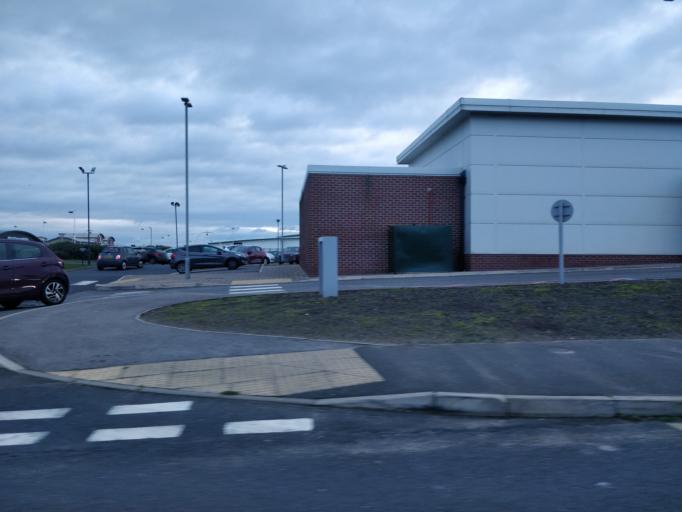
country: GB
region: England
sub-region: Sefton
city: Southport
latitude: 53.6540
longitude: -3.0126
